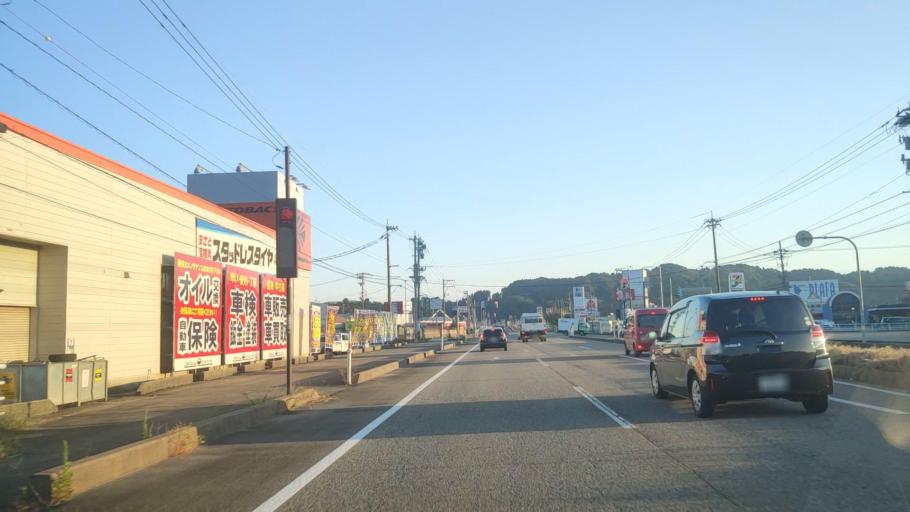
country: JP
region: Toyama
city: Himi
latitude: 36.8649
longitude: 136.9756
